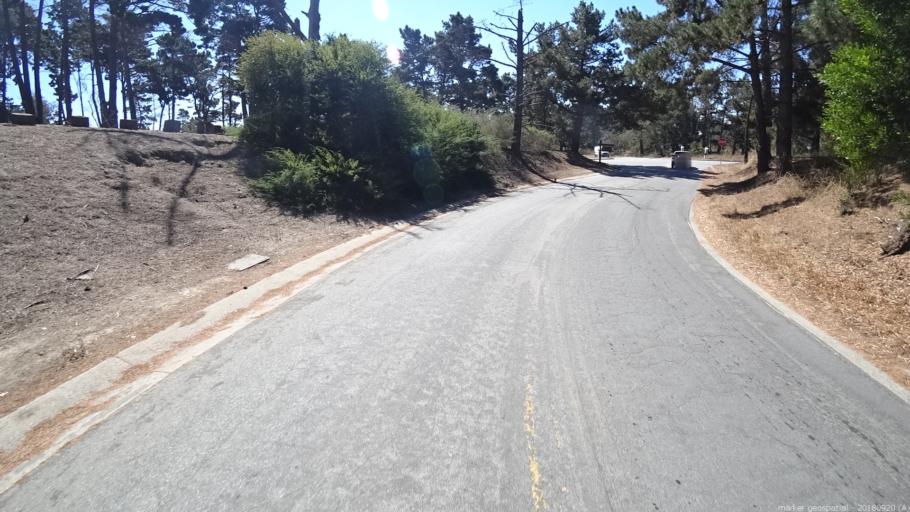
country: US
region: California
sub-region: Monterey County
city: Carmel-by-the-Sea
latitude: 36.5685
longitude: -121.9108
